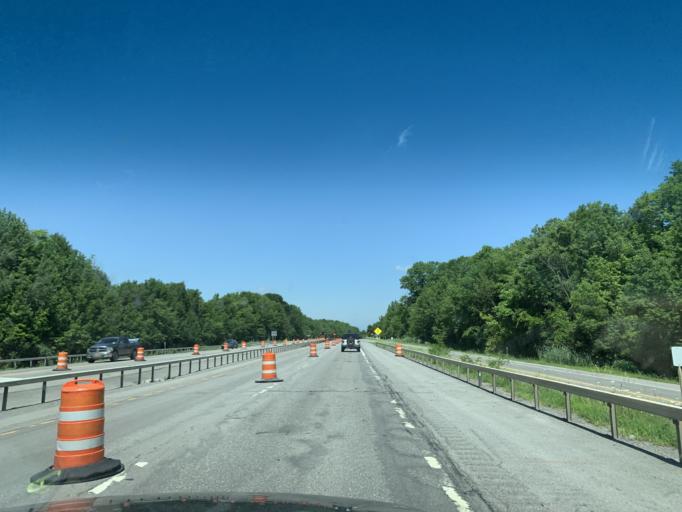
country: US
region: New York
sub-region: Oneida County
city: Chadwicks
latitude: 43.0229
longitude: -75.2611
